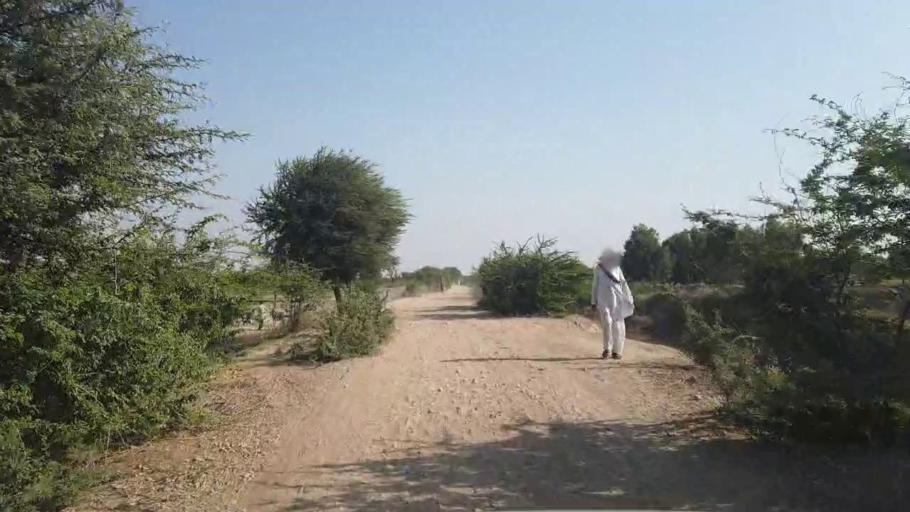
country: PK
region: Sindh
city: Chor
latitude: 25.5206
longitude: 69.6737
